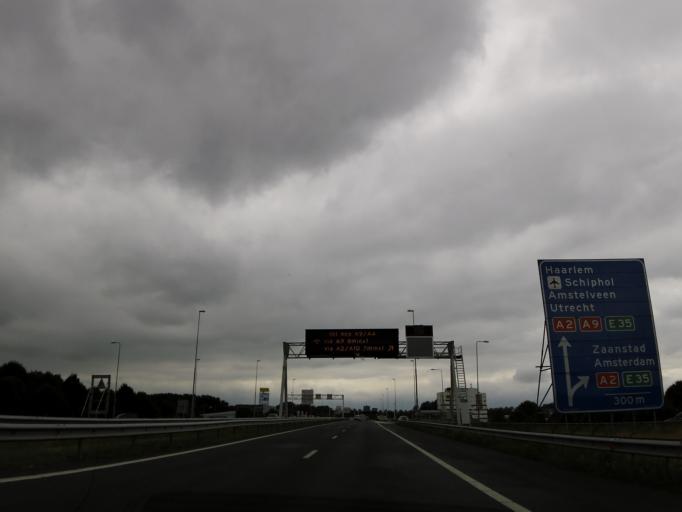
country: NL
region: North Holland
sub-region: Gemeente Amsterdam
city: Amsterdam-Zuidoost
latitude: 52.3006
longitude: 4.9499
